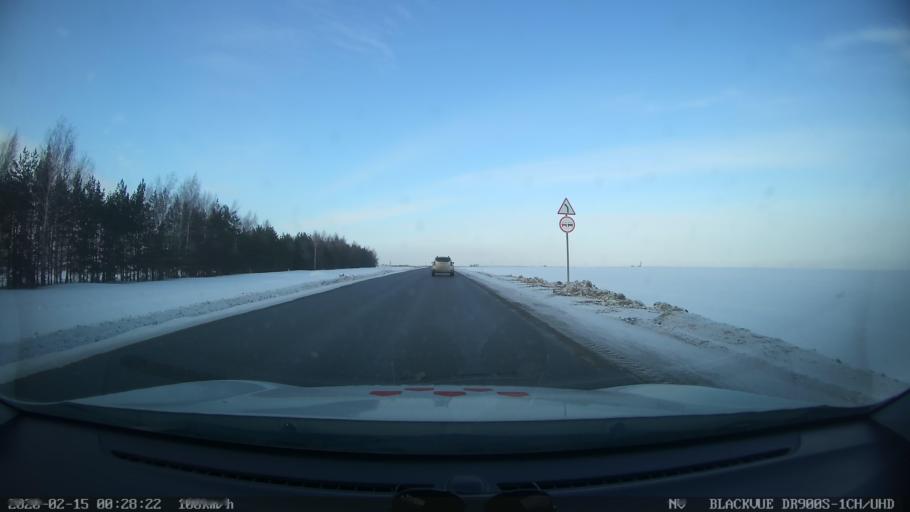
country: RU
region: Tatarstan
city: Verkhniy Uslon
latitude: 55.6415
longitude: 48.8756
